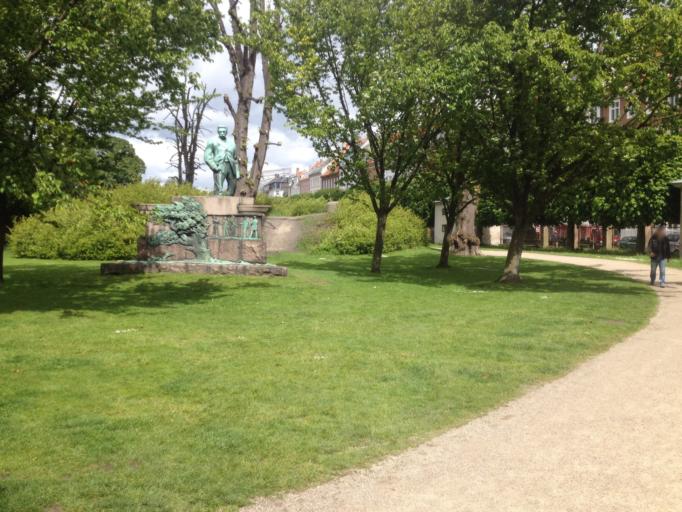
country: DK
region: Capital Region
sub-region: Kobenhavn
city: Copenhagen
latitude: 55.6832
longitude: 12.5805
